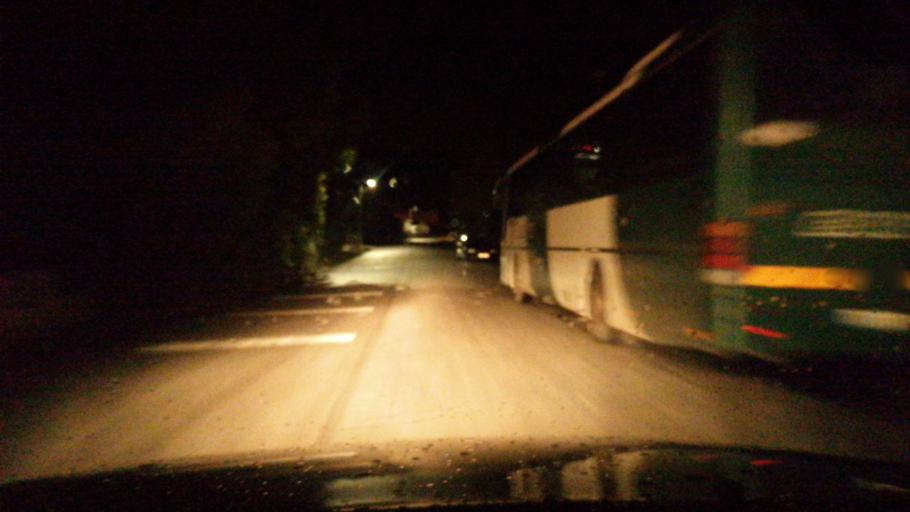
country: PT
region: Viseu
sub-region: Moimenta da Beira
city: Moimenta da Beira
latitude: 41.0413
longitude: -7.6401
